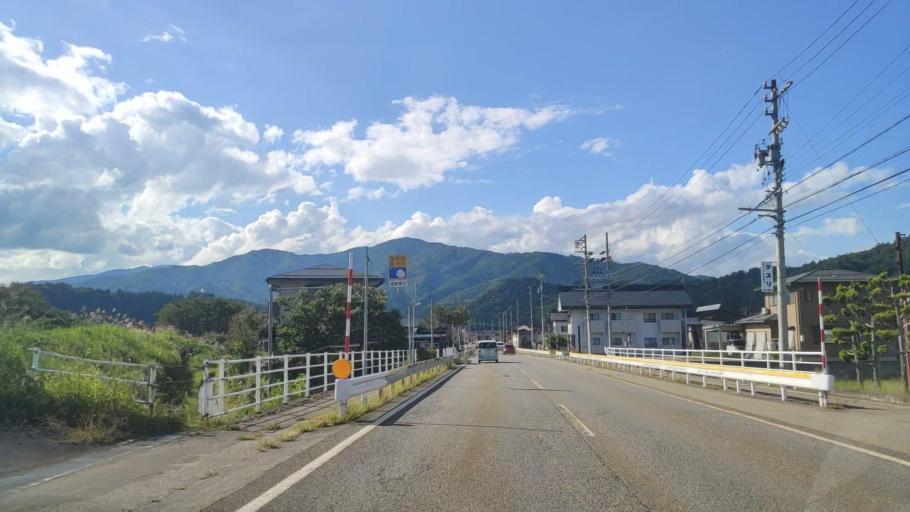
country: JP
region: Gifu
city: Takayama
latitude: 36.2576
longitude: 137.1529
